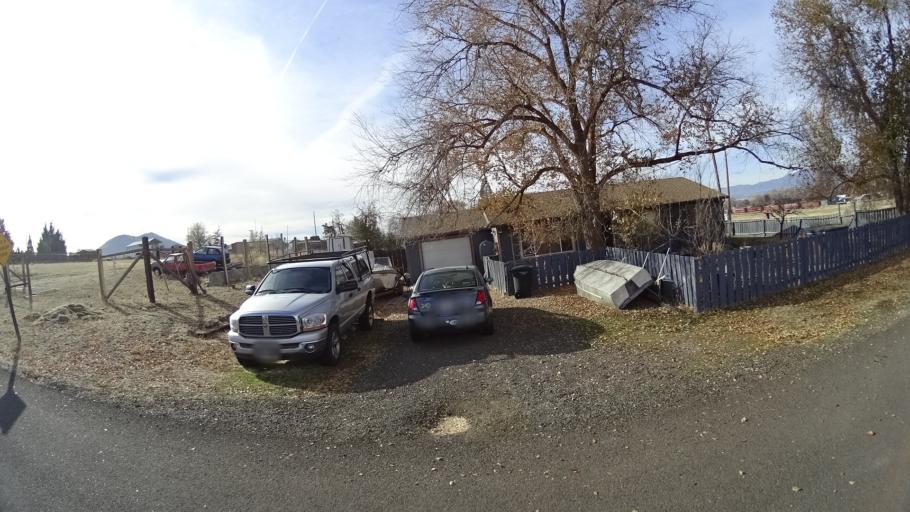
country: US
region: California
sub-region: Siskiyou County
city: Montague
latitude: 41.7327
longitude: -122.5201
